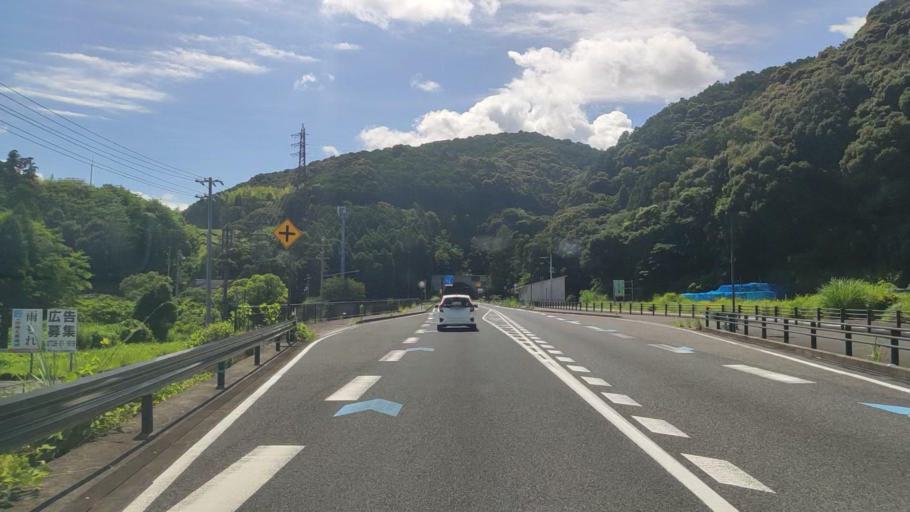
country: JP
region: Wakayama
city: Shingu
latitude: 33.7405
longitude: 135.9965
